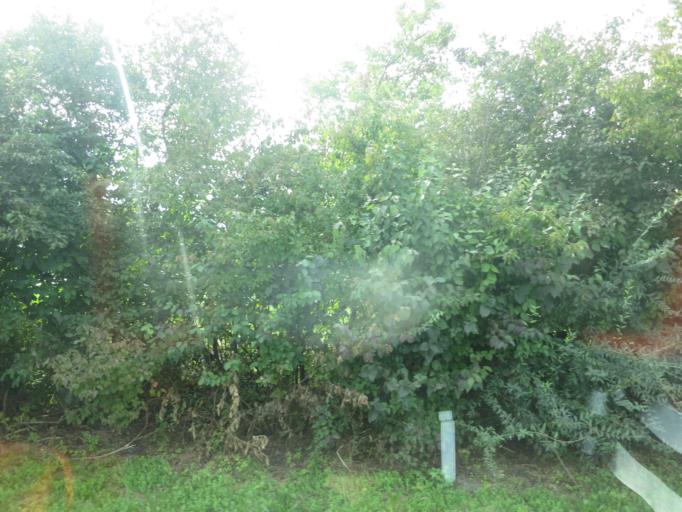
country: CH
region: Schwyz
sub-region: Bezirk March
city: Reichenburg
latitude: 47.1846
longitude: 8.9788
